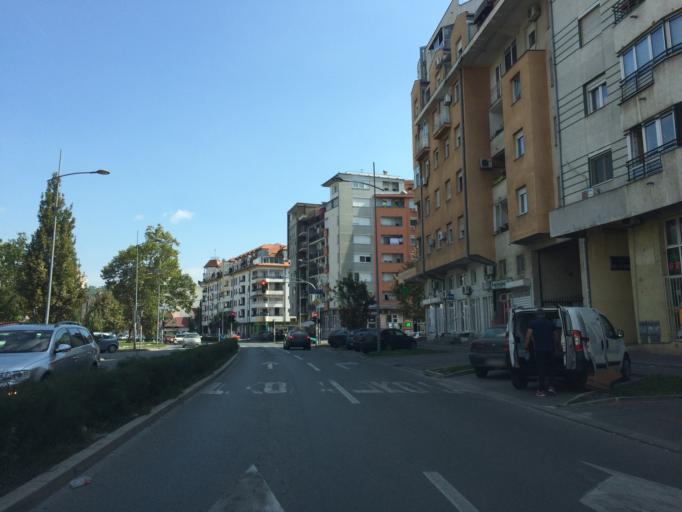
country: RS
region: Autonomna Pokrajina Vojvodina
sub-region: Juznobacki Okrug
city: Novi Sad
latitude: 45.2485
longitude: 19.8339
